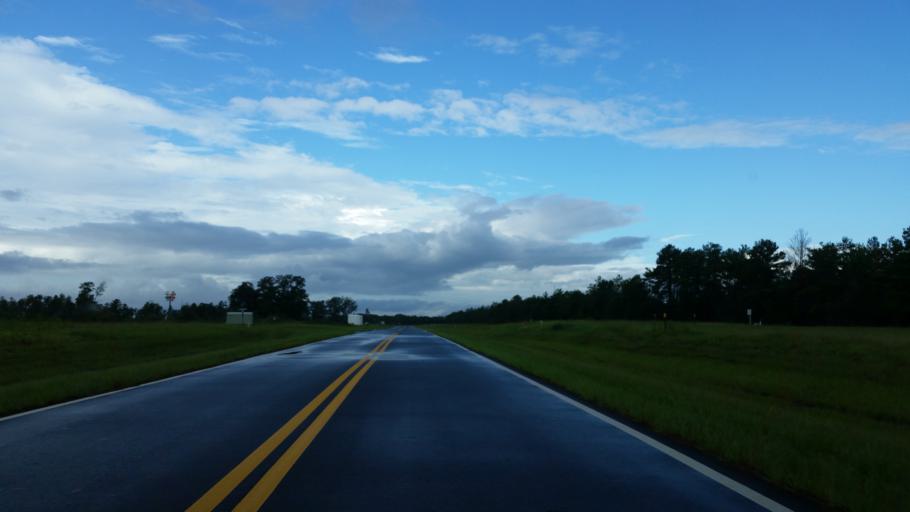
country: US
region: Florida
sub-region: Walton County
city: DeFuniak Springs
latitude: 30.7381
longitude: -86.3371
